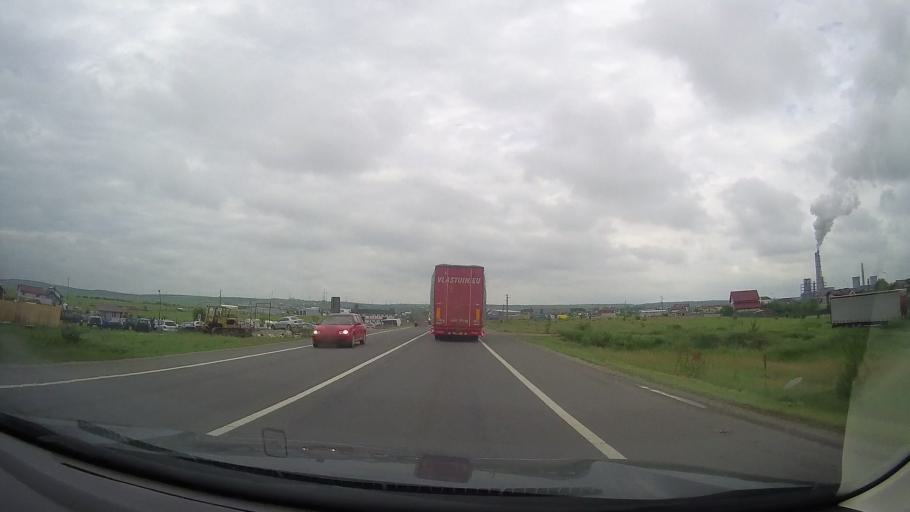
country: RO
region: Dolj
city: Craiova
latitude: 44.3492
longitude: 23.7965
